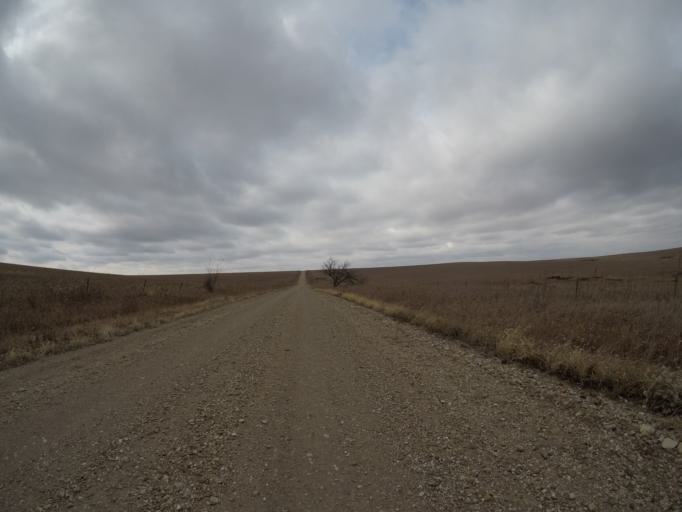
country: US
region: Kansas
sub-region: Morris County
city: Council Grove
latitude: 38.7244
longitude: -96.2006
